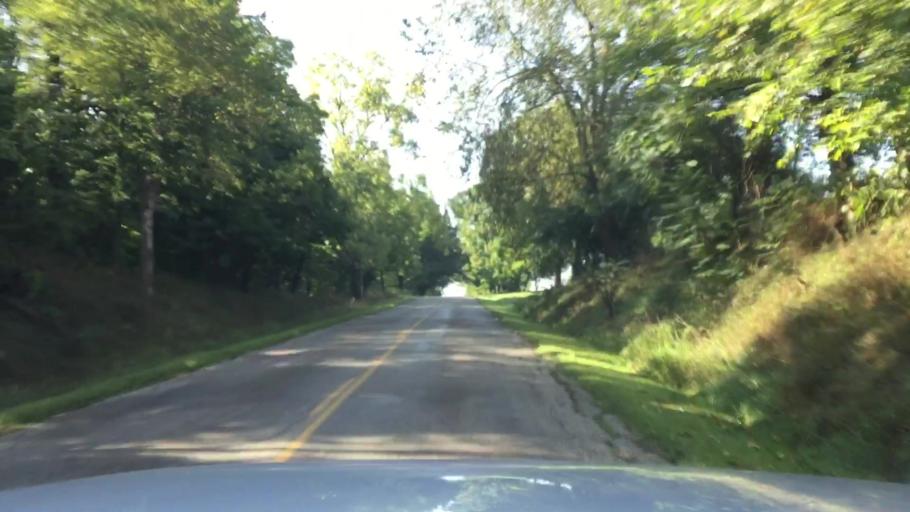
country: US
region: Michigan
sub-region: Lenawee County
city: Hudson
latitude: 41.9224
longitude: -84.4205
